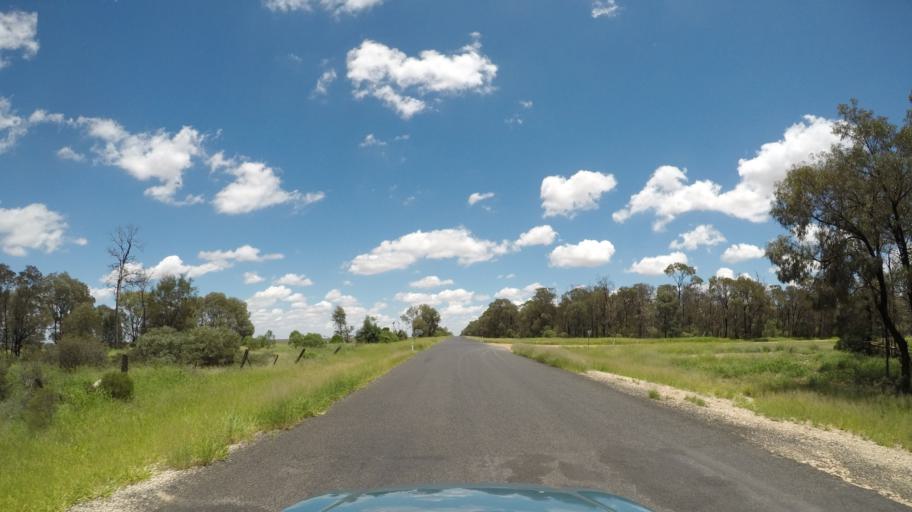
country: AU
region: Queensland
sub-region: Goondiwindi
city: Goondiwindi
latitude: -28.1612
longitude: 150.4097
